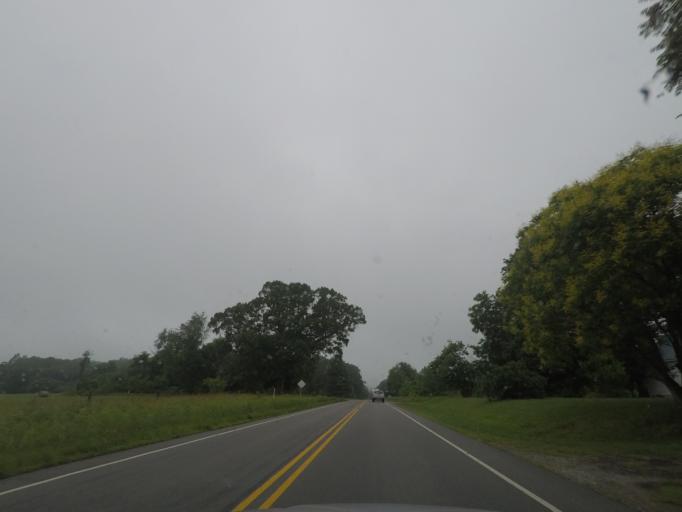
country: US
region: Virginia
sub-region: Buckingham County
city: Buckingham
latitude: 37.4464
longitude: -78.4557
